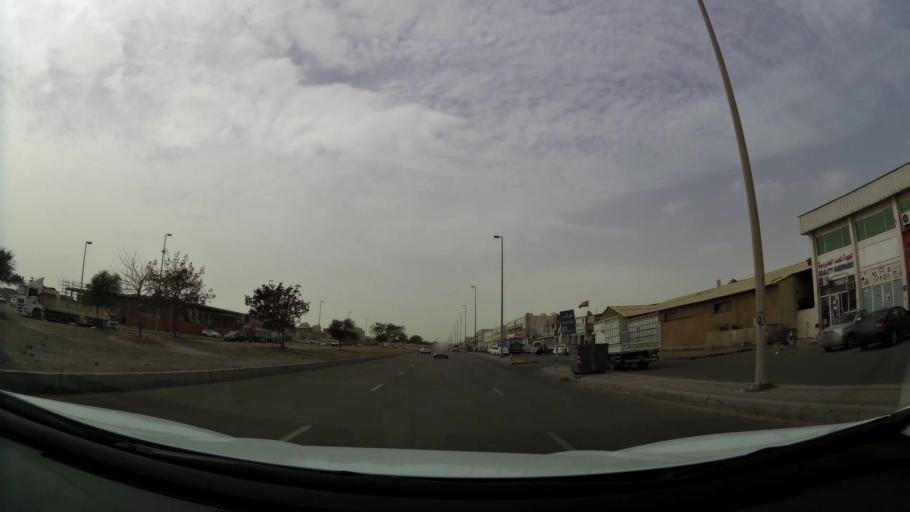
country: AE
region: Abu Dhabi
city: Abu Dhabi
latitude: 24.3688
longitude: 54.5106
